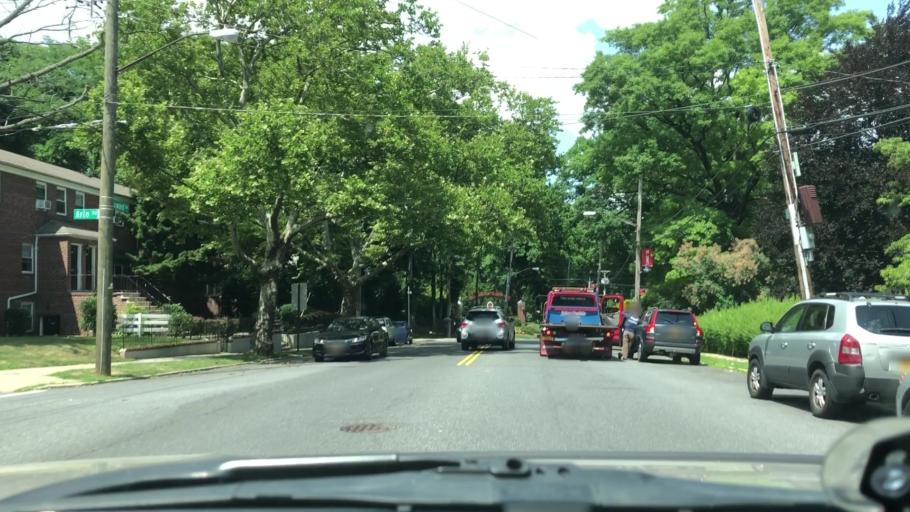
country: US
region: New Jersey
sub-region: Hudson County
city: Bayonne
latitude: 40.6194
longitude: -74.0902
